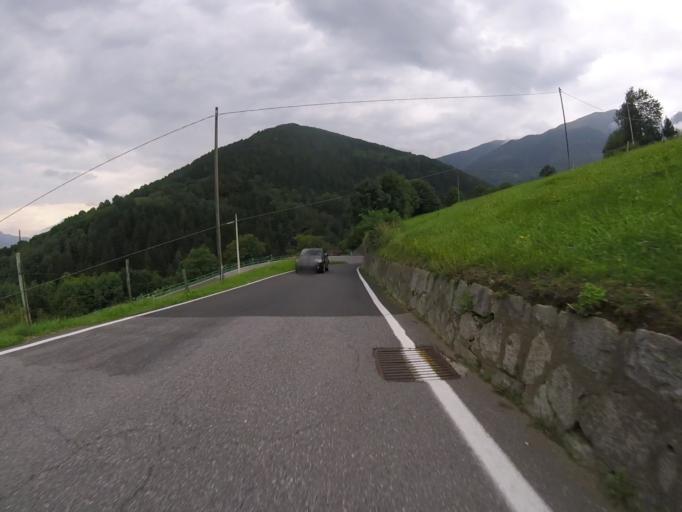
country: IT
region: Lombardy
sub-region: Provincia di Brescia
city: Monno
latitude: 46.2093
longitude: 10.3455
